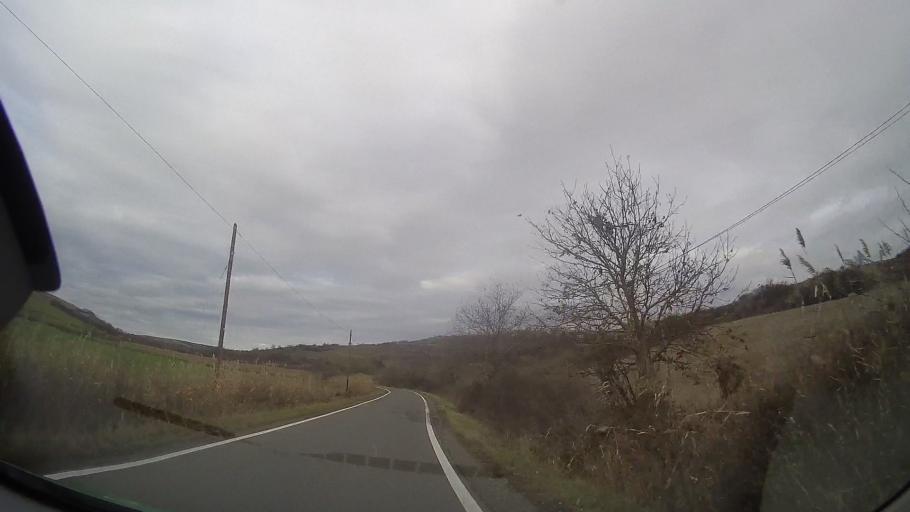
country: RO
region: Mures
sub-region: Comuna Cozma
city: Cozma
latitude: 46.7998
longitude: 24.5368
